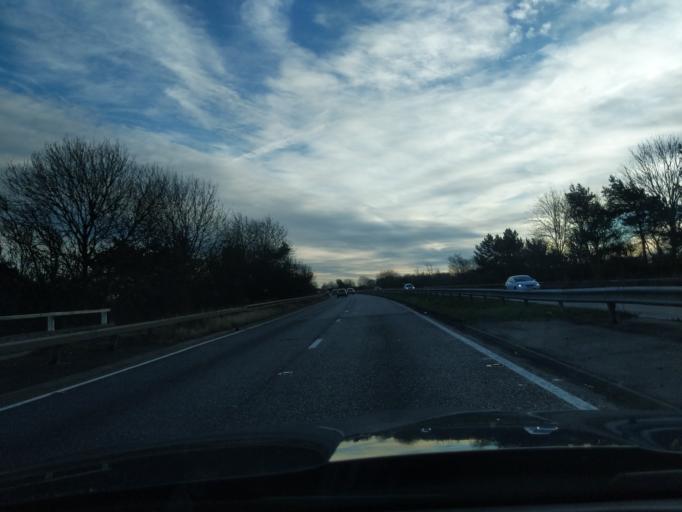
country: GB
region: England
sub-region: Northumberland
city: Seghill
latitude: 55.0457
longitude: -1.5514
